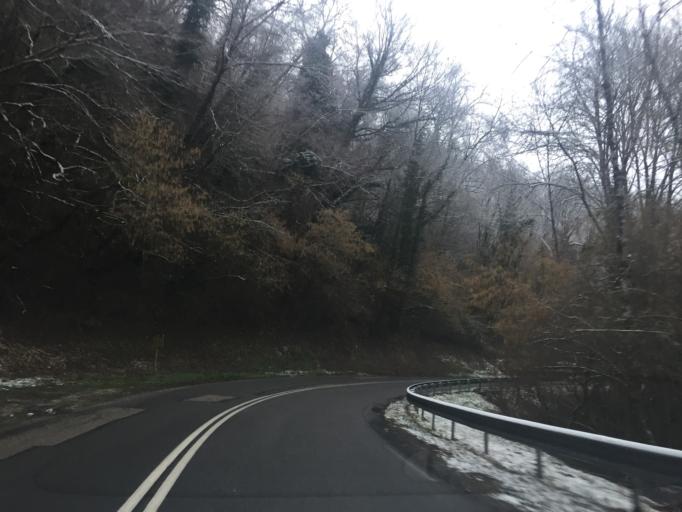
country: FR
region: Rhone-Alpes
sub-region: Departement de la Savoie
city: Gresy-sur-Aix
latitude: 45.7300
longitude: 5.9503
